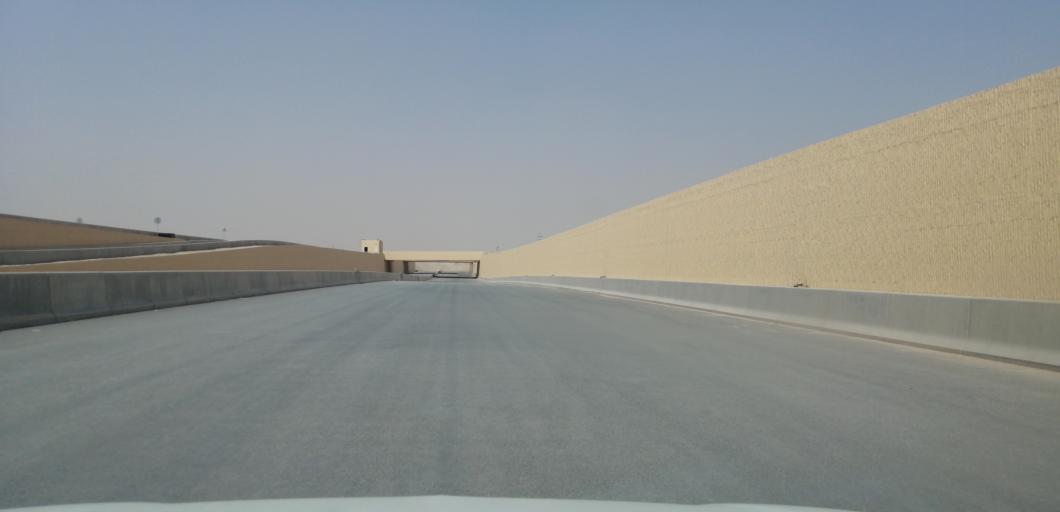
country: KW
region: Muhafazat al Jahra'
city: Al Jahra'
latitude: 29.4538
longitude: 47.5531
